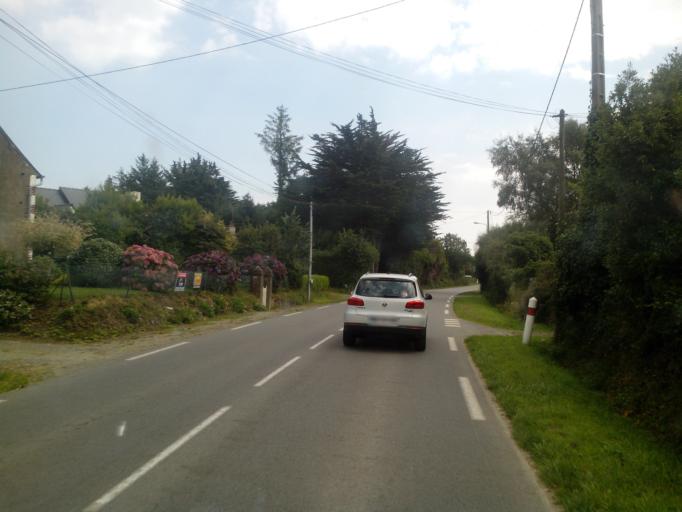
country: FR
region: Brittany
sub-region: Departement des Cotes-d'Armor
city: Plouha
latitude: 48.7004
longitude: -2.9451
